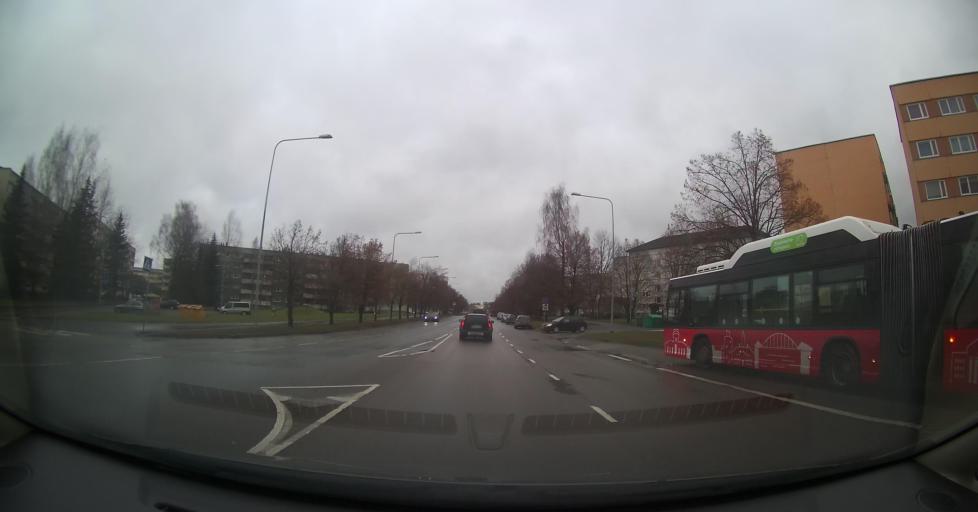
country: EE
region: Tartu
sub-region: Tartu linn
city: Tartu
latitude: 58.3714
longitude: 26.7662
